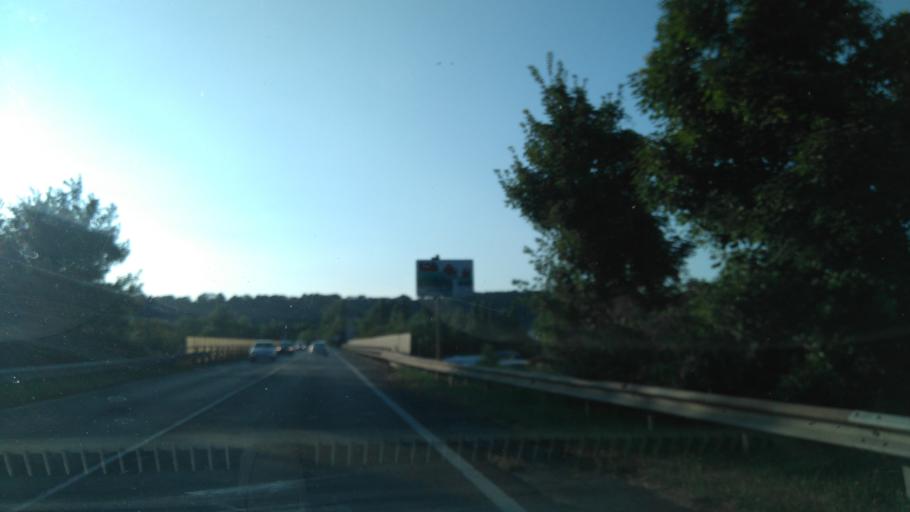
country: FR
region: Picardie
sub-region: Departement de l'Oise
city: Montataire
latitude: 49.2546
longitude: 2.4544
